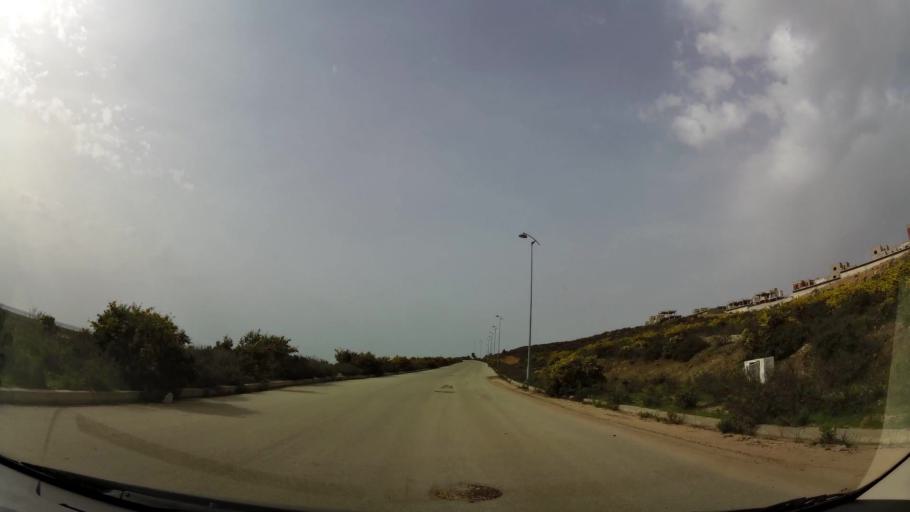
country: MA
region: Tanger-Tetouan
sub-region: Tanger-Assilah
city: Boukhalef
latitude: 35.6965
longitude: -5.9412
